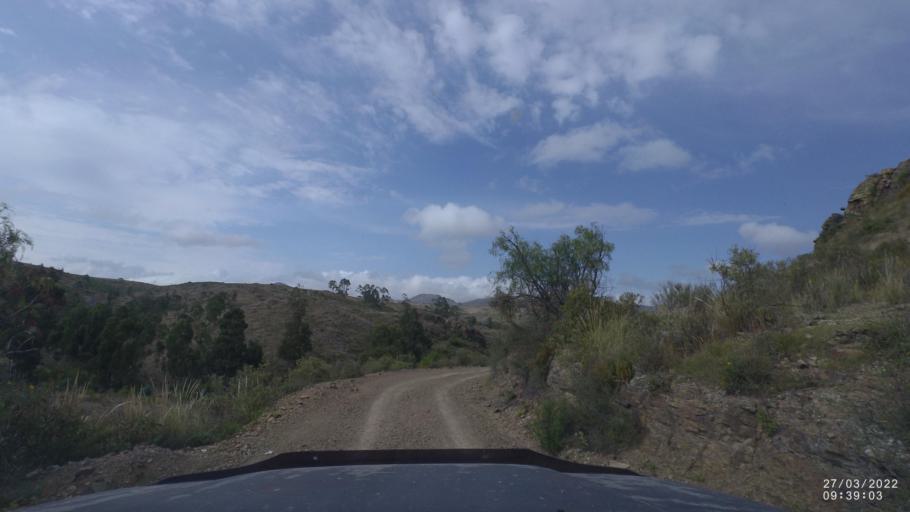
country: BO
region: Cochabamba
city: Cliza
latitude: -17.7486
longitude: -65.8970
